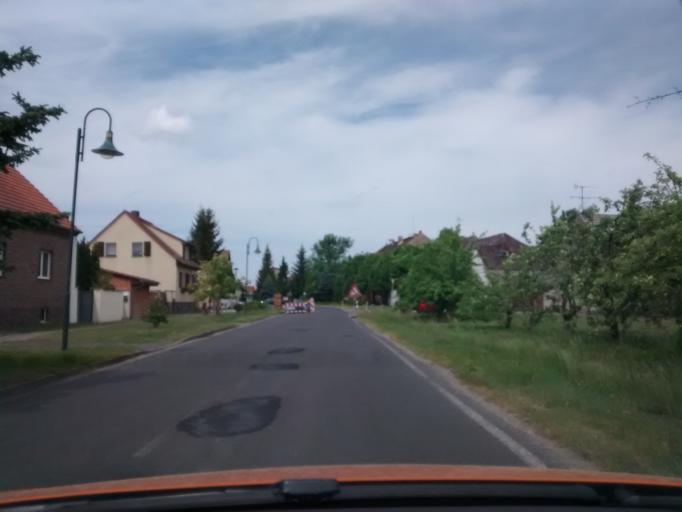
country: DE
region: Saxony-Anhalt
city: Holzdorf
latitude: 51.8408
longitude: 13.2191
